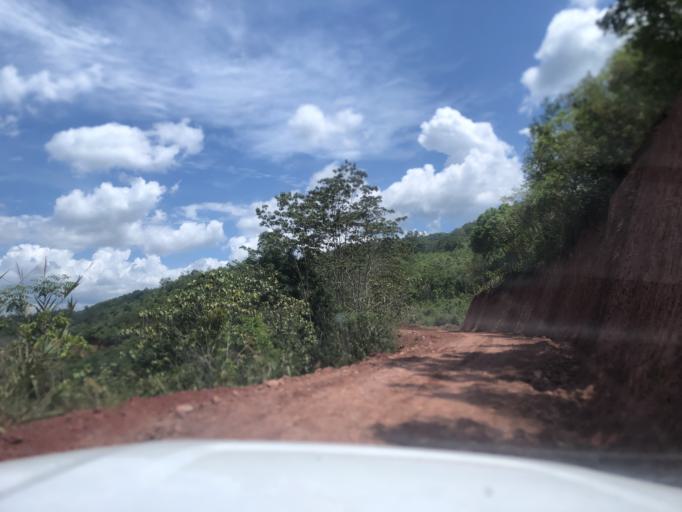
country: CN
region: Yunnan
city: Menglie
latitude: 22.2318
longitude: 101.6198
